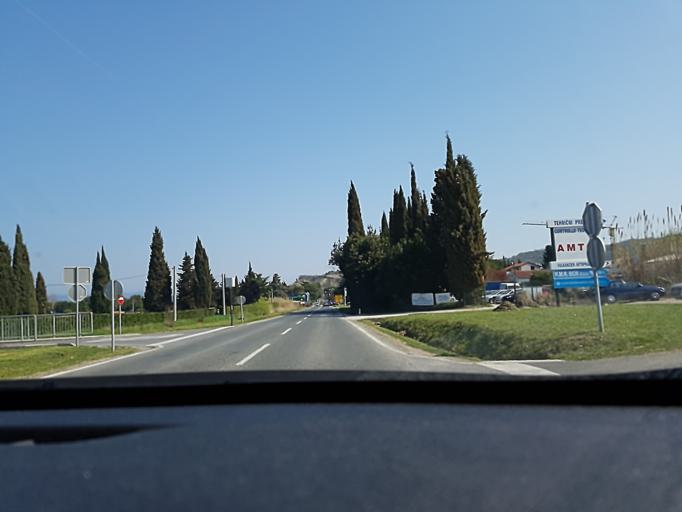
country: SI
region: Izola-Isola
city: Izola
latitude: 45.5361
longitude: 13.6661
